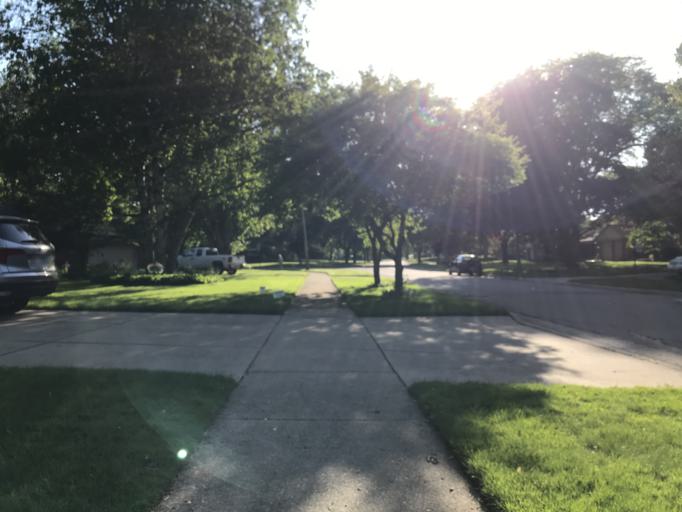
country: US
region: Michigan
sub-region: Oakland County
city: Farmington
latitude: 42.4618
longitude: -83.3807
